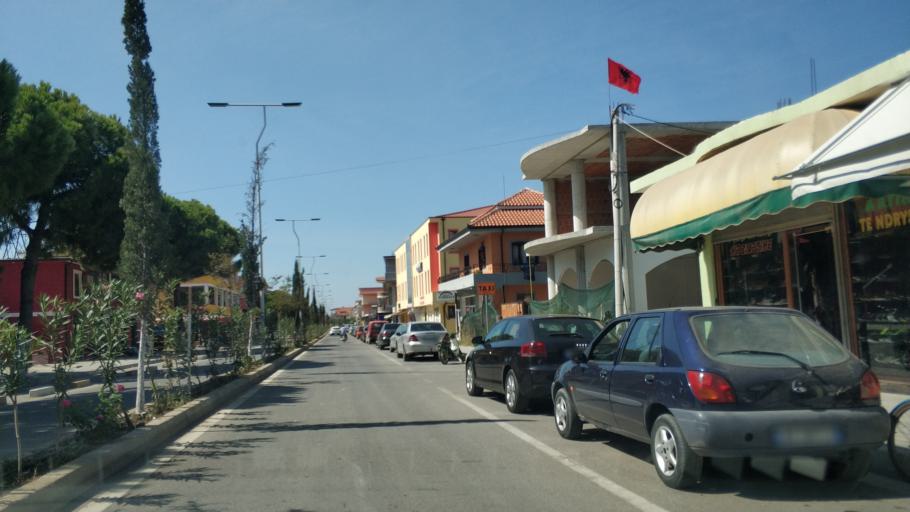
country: AL
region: Fier
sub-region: Rrethi i Lushnjes
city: Divjake
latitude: 40.9962
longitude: 19.5320
